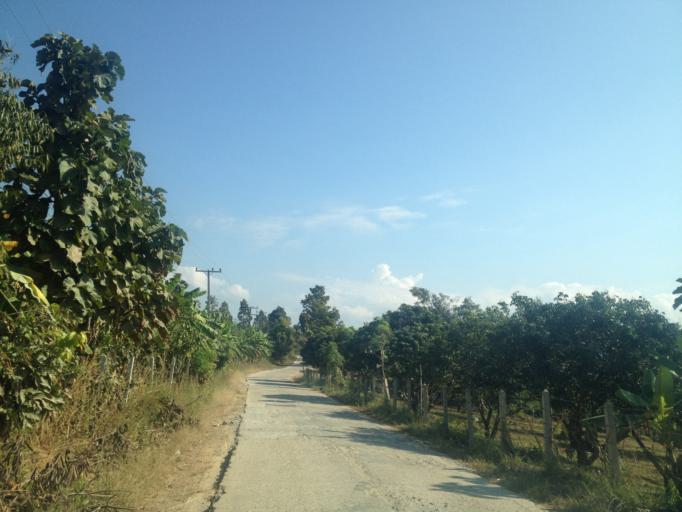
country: TH
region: Mae Hong Son
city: Ban Huai I Huak
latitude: 18.1012
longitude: 98.2148
